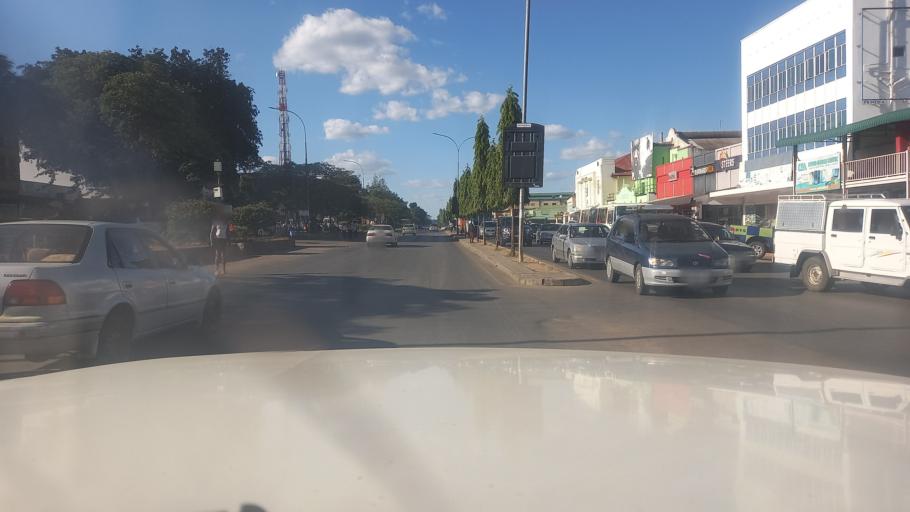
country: ZM
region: Southern
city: Livingstone
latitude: -17.8472
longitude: 25.8567
